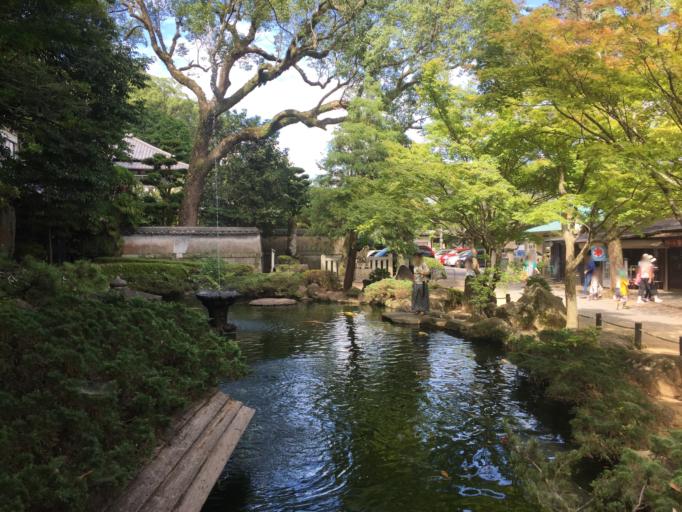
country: JP
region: Nagasaki
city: Nagasaki-shi
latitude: 32.7537
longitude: 129.8814
